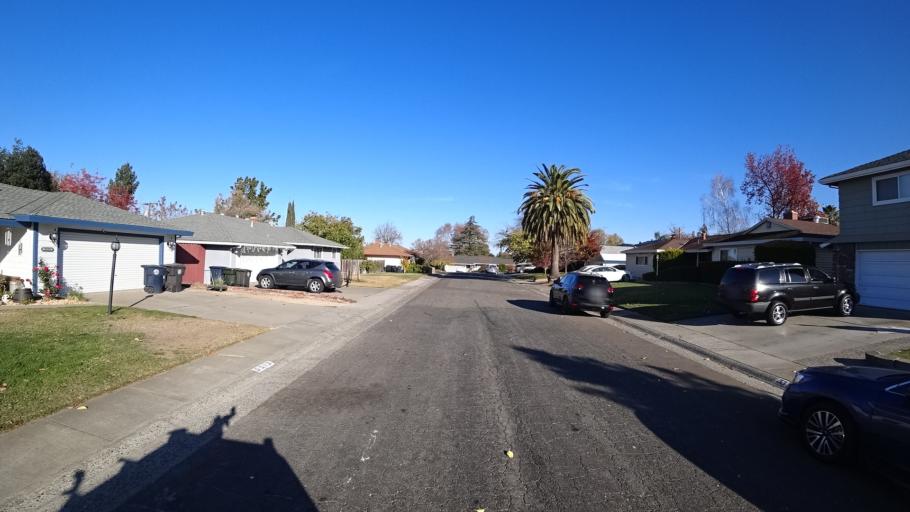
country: US
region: California
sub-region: Sacramento County
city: Fair Oaks
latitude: 38.6661
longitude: -121.2934
